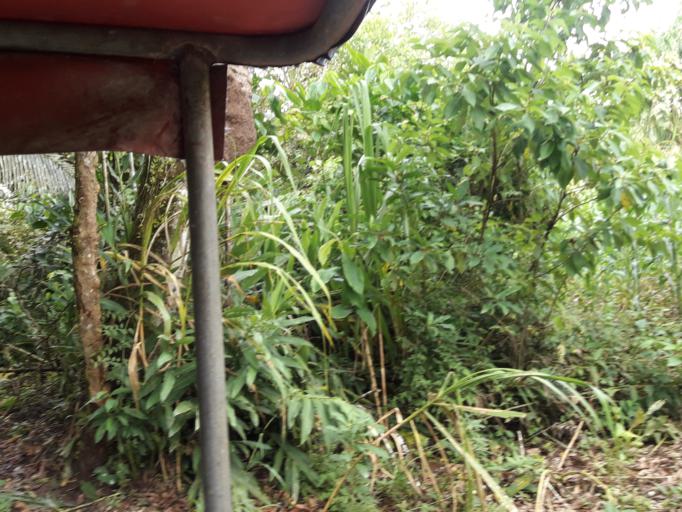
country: EC
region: Napo
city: Tena
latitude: -1.0705
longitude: -77.7954
